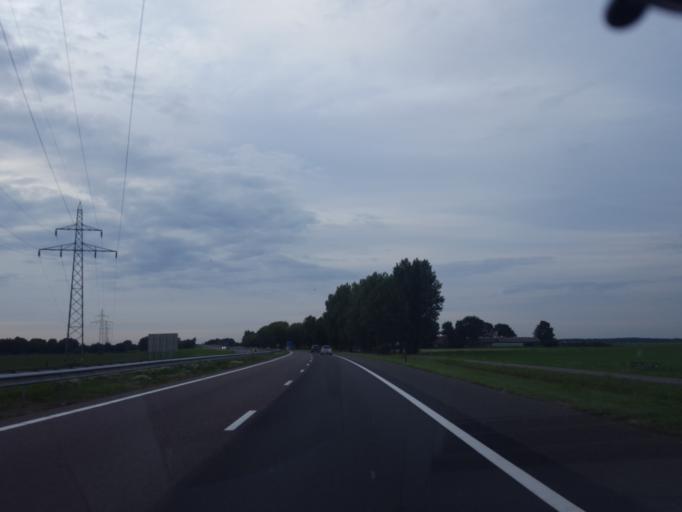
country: NL
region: Drenthe
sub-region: Gemeente Meppel
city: Meppel
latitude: 52.7191
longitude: 6.2054
